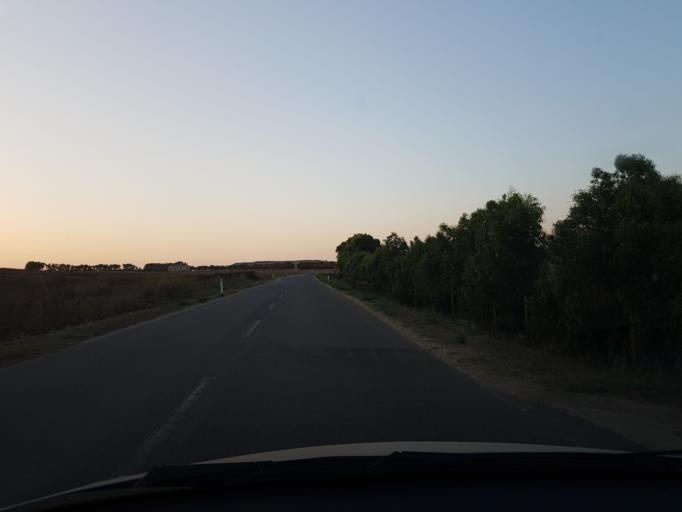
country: IT
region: Sardinia
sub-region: Provincia di Oristano
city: Nurachi
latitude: 39.9649
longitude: 8.4534
